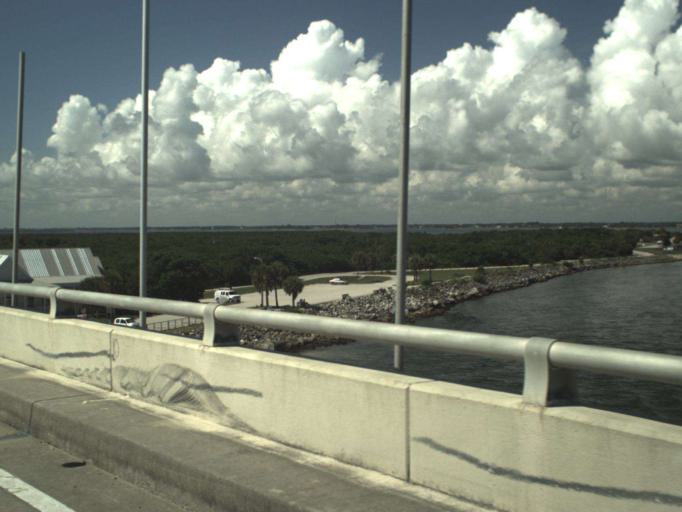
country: US
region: Florida
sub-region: Indian River County
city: Sebastian
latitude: 27.8601
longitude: -80.4484
